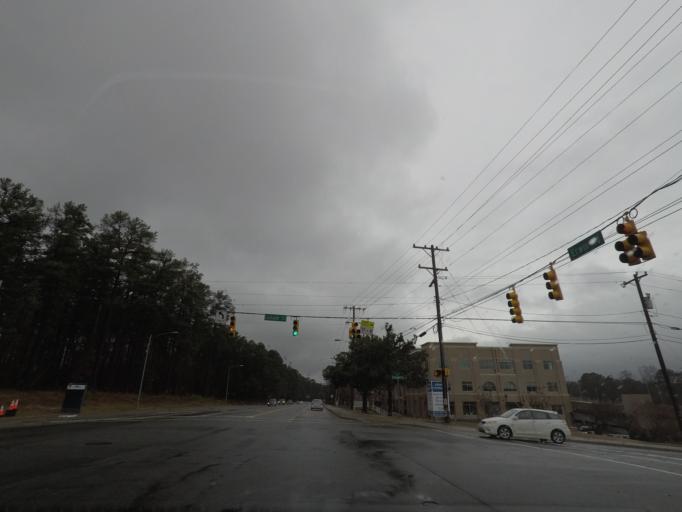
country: US
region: North Carolina
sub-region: Durham County
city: Durham
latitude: 36.0077
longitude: -78.9462
